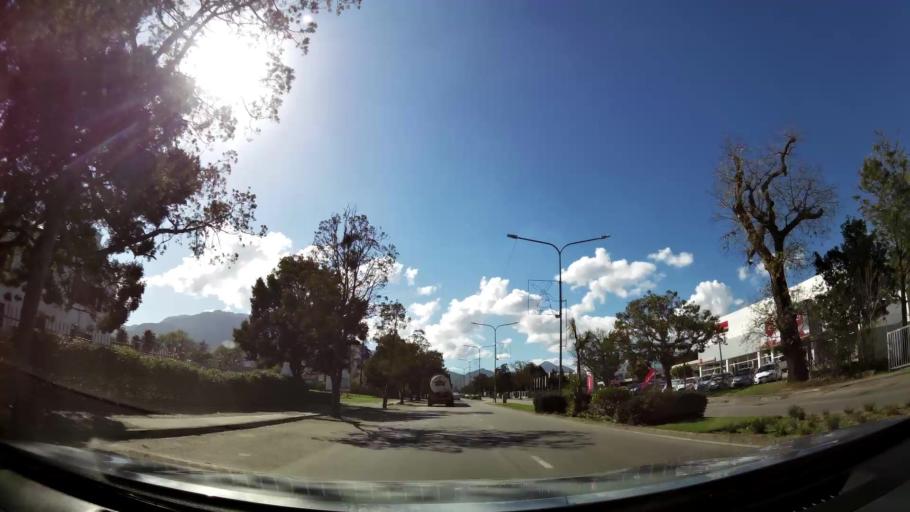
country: ZA
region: Western Cape
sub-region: Eden District Municipality
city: George
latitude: -33.9685
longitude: 22.4491
